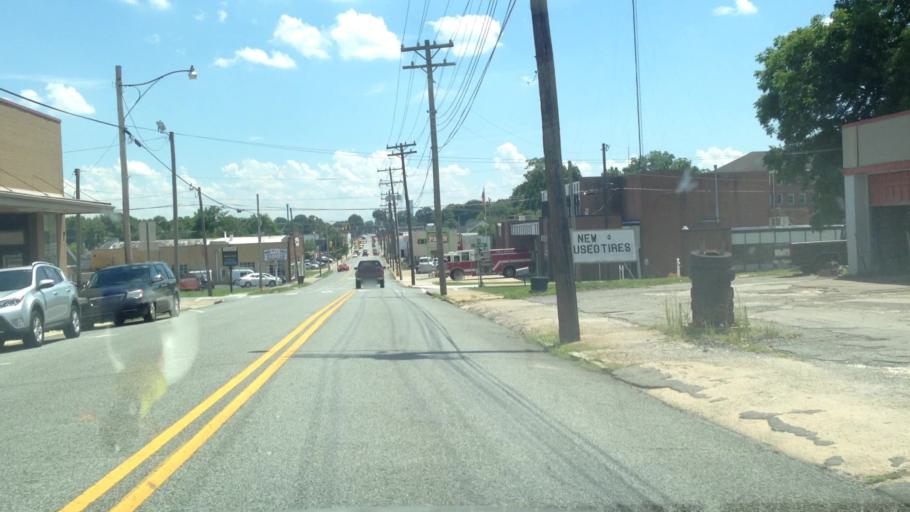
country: US
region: North Carolina
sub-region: Rockingham County
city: Reidsville
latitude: 36.3581
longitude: -79.6644
